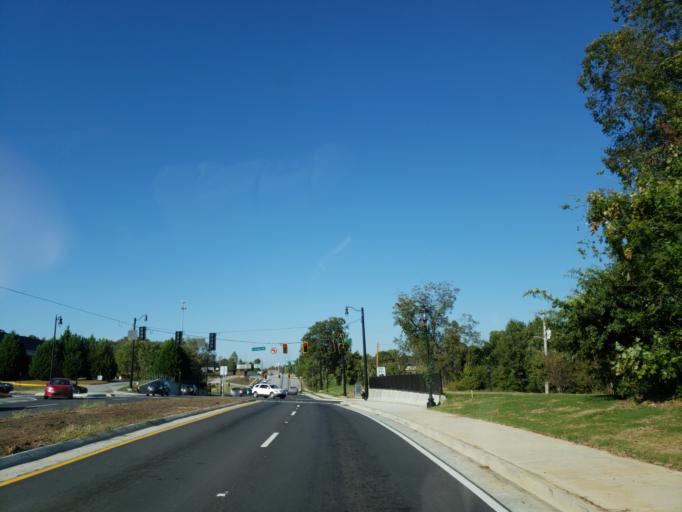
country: US
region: Georgia
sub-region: Gwinnett County
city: Lawrenceville
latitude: 33.9559
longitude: -83.9857
